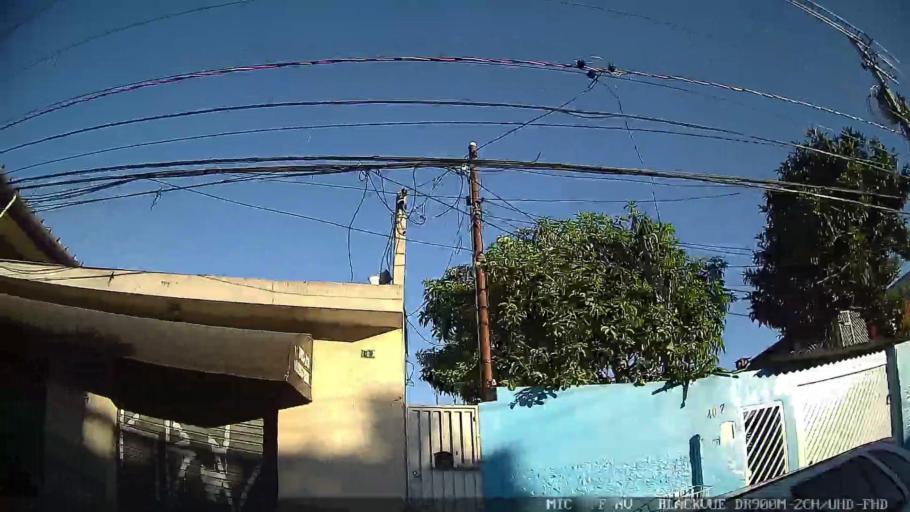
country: BR
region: Sao Paulo
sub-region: Guarulhos
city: Guarulhos
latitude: -23.5424
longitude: -46.5062
